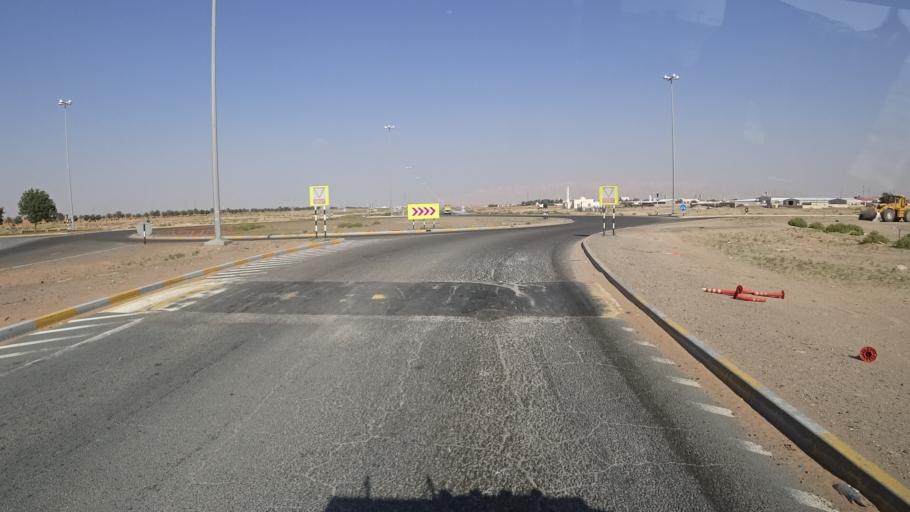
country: AE
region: Abu Dhabi
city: Al Ain
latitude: 24.0460
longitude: 55.5983
